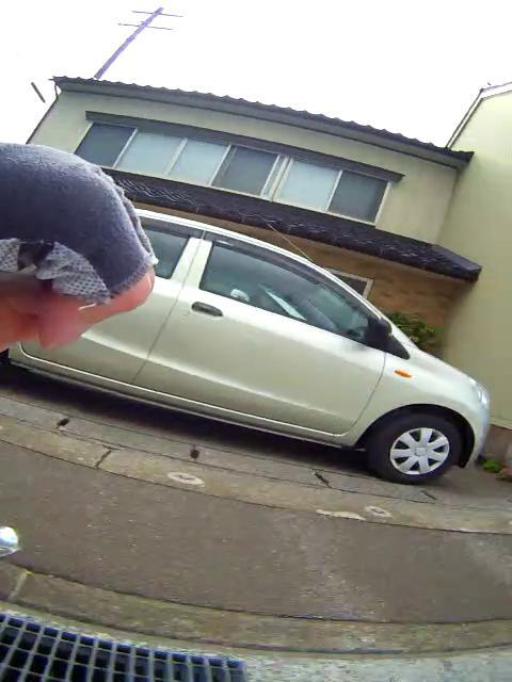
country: JP
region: Toyama
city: Takaoka
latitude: 36.7383
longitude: 137.0035
